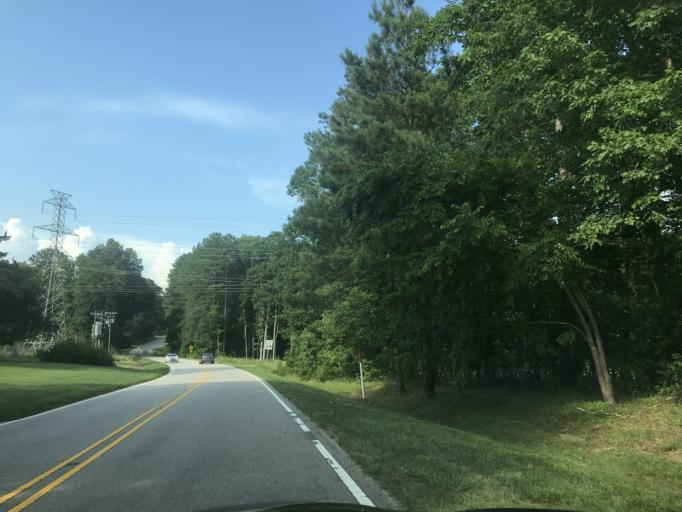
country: US
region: North Carolina
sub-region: Wake County
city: Knightdale
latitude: 35.8152
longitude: -78.5594
